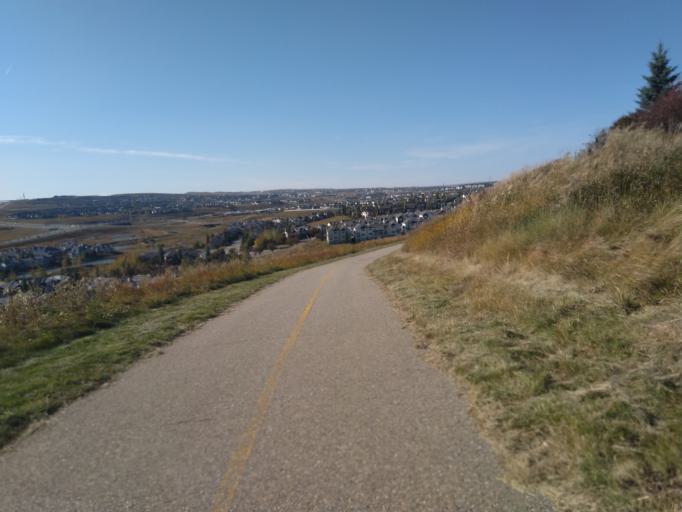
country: CA
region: Alberta
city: Calgary
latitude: 51.1562
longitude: -114.0950
